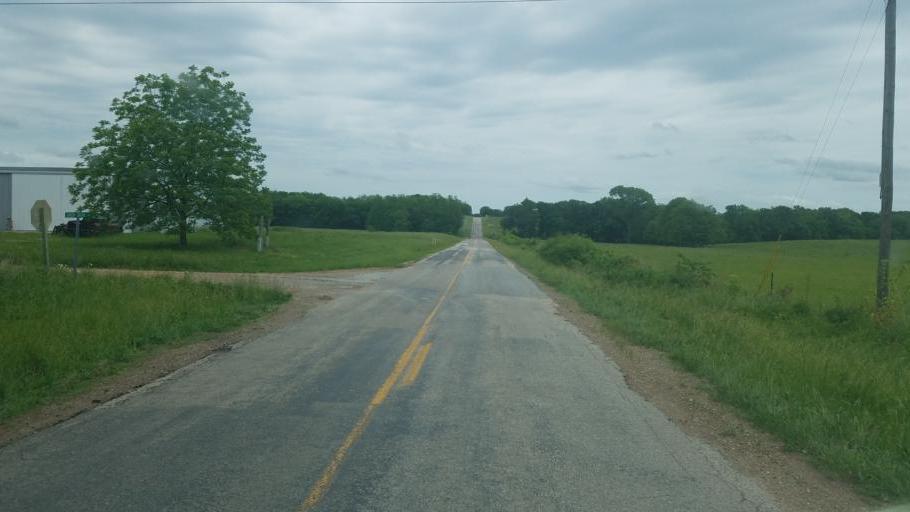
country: US
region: Missouri
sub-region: Moniteau County
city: Tipton
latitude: 38.5663
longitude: -92.7278
